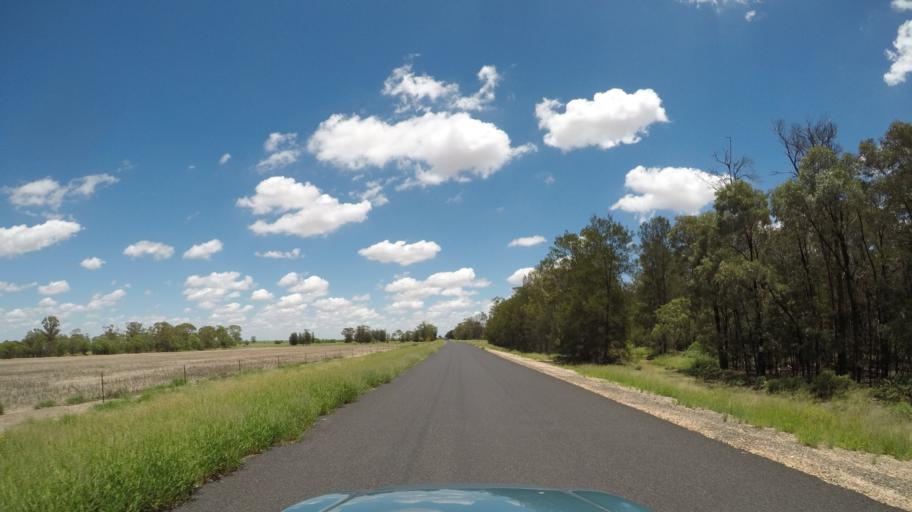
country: AU
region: Queensland
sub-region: Goondiwindi
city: Goondiwindi
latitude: -28.1561
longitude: 150.3763
